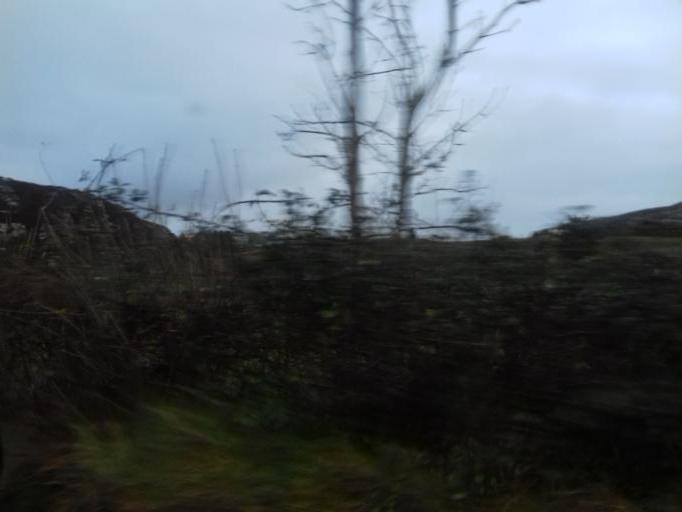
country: IE
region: Ulster
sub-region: County Donegal
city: Ramelton
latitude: 55.2248
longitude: -7.6240
